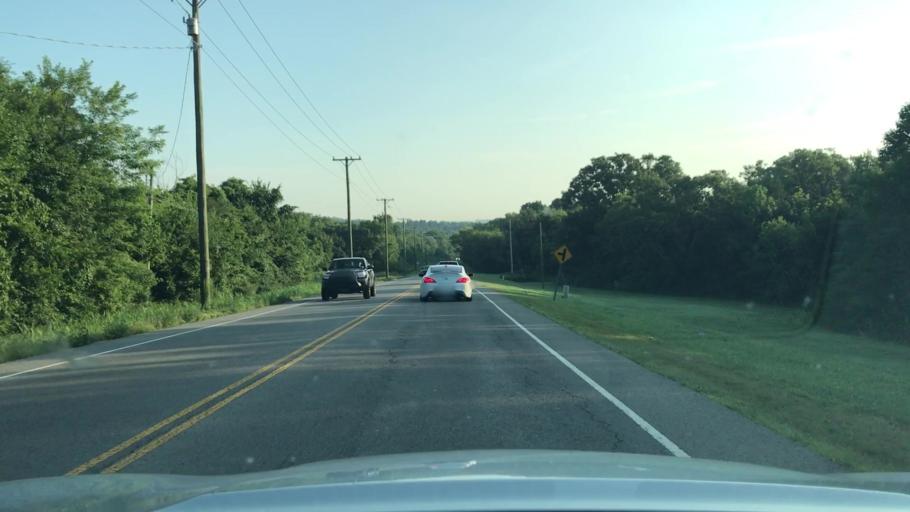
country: US
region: Tennessee
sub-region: Rutherford County
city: La Vergne
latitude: 35.9935
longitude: -86.6245
